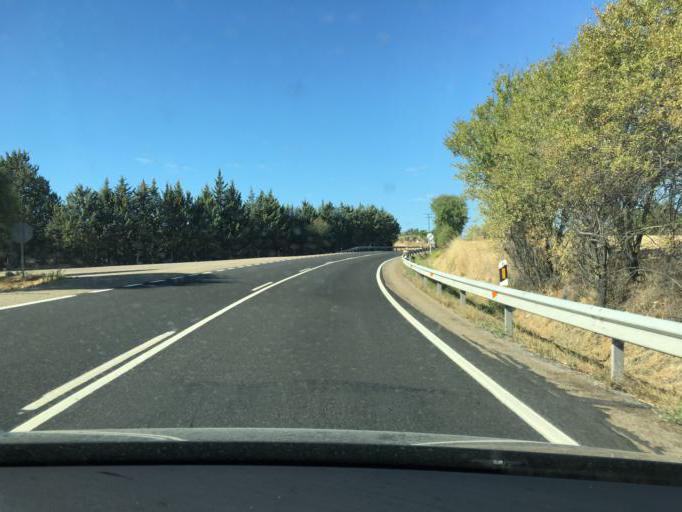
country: ES
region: Madrid
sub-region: Provincia de Madrid
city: Reduena
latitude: 40.8179
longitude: -3.5693
